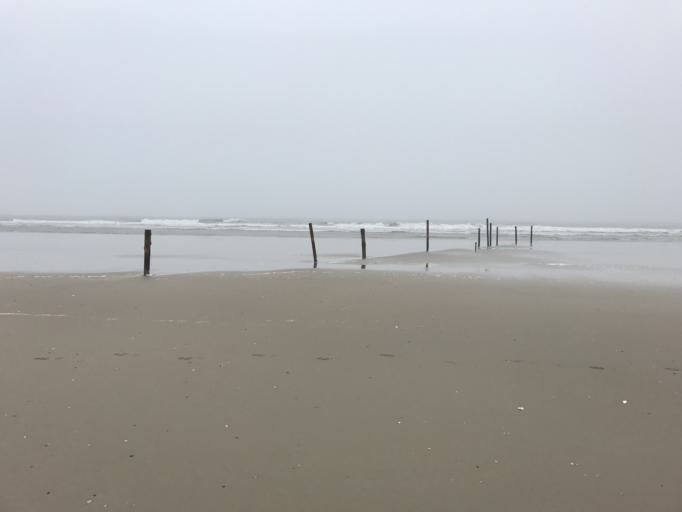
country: DE
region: Lower Saxony
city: Borkum
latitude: 53.5964
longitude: 6.6418
